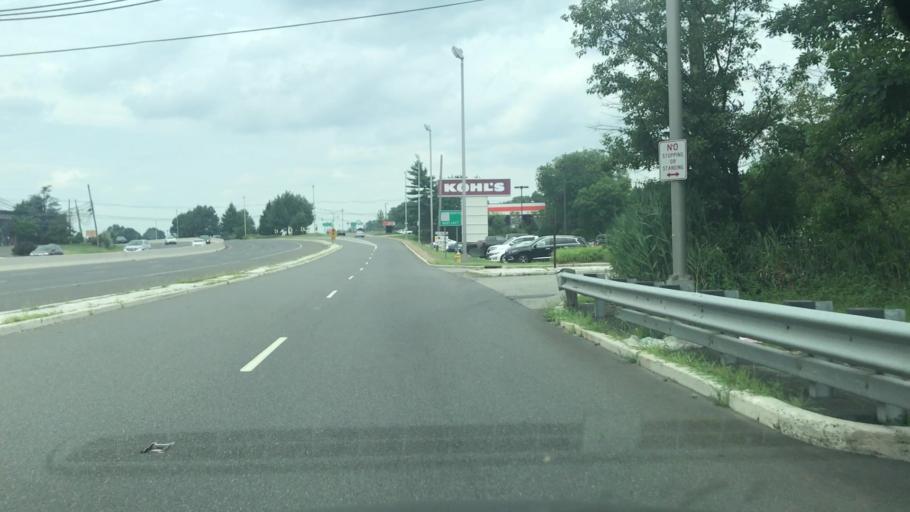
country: US
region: New Jersey
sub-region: Passaic County
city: Wayne
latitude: 40.9445
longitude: -74.2722
